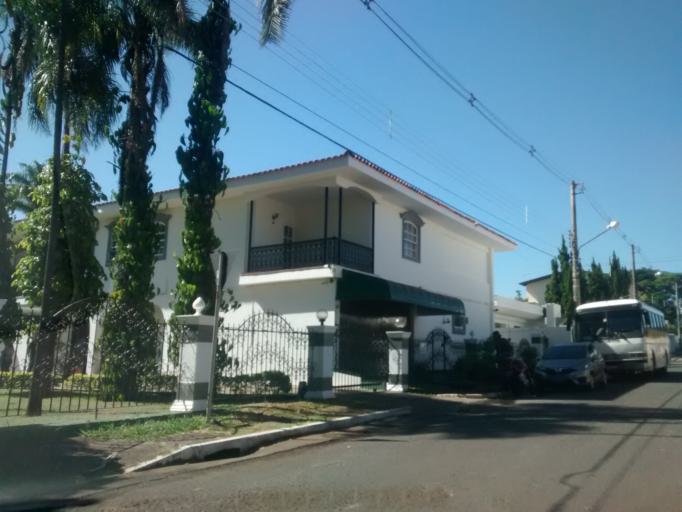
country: BR
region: Federal District
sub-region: Brasilia
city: Brasilia
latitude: -15.8482
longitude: -47.9029
